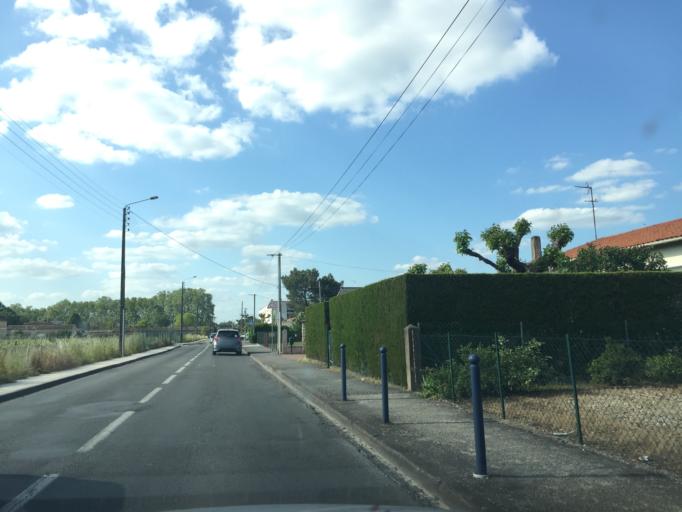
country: FR
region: Aquitaine
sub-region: Departement de la Gironde
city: Libourne
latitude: 44.9312
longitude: -0.2407
